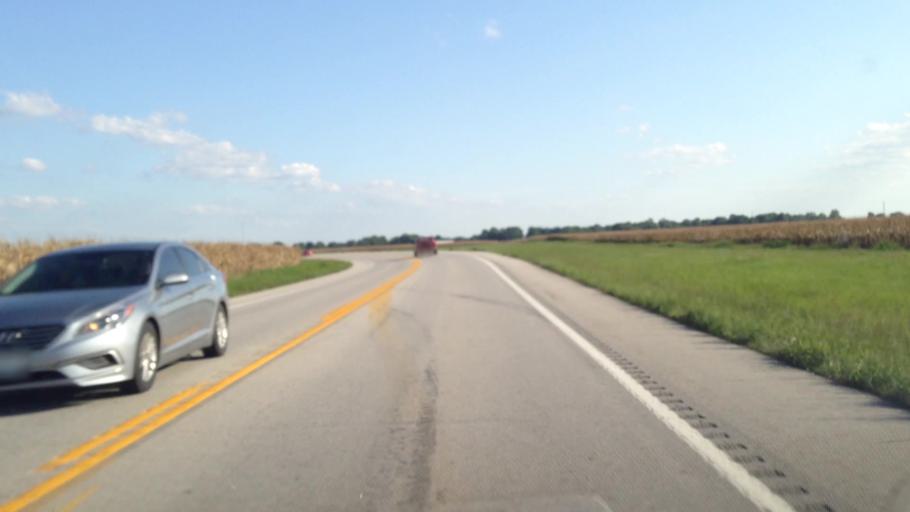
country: US
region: Missouri
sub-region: Jasper County
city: Carl Junction
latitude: 37.2872
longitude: -94.6077
